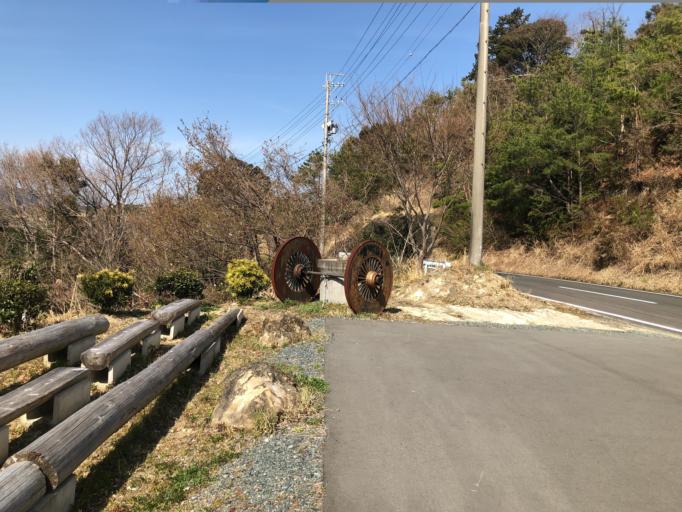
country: JP
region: Shizuoka
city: Kanaya
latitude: 34.8288
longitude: 138.0821
